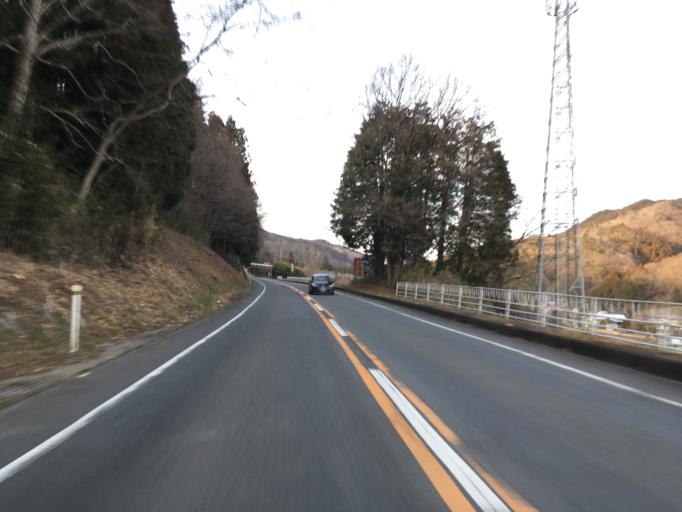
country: JP
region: Ibaraki
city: Daigo
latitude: 36.8223
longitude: 140.3791
